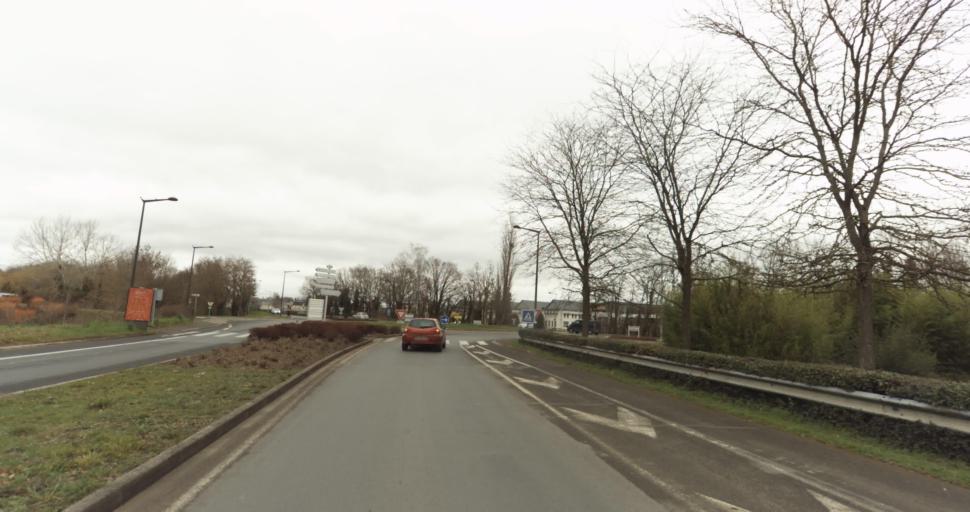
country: FR
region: Pays de la Loire
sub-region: Departement de Maine-et-Loire
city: Saumur
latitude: 47.2497
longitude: -0.0791
